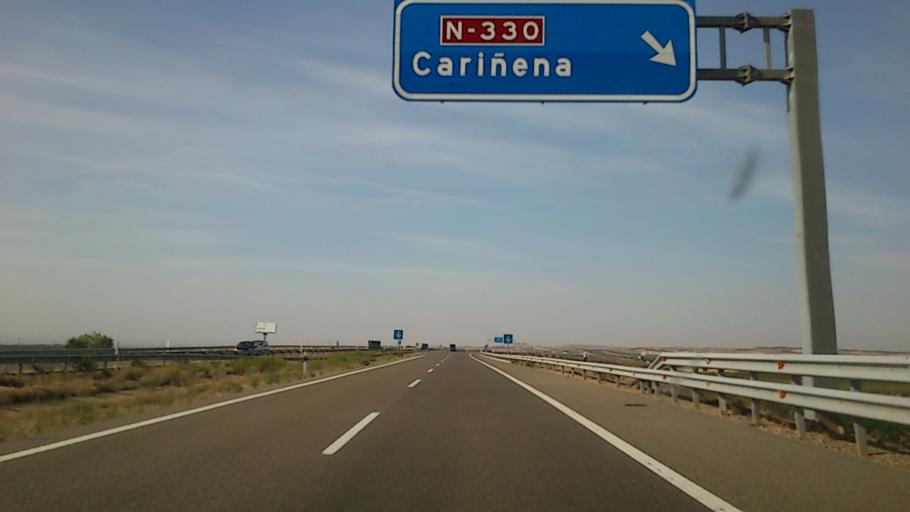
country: ES
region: Aragon
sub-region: Provincia de Zaragoza
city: Carinena
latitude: 41.3620
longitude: -1.2029
